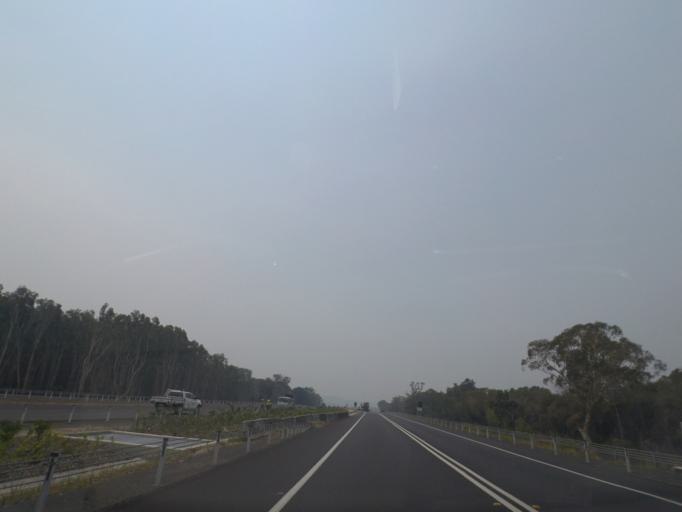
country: AU
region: New South Wales
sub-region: Ballina
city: Ballina
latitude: -28.9115
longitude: 153.4788
